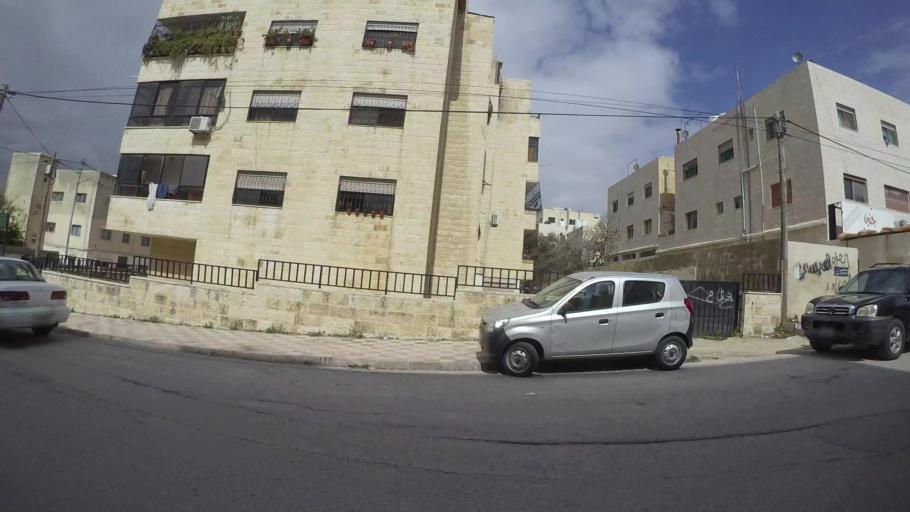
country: JO
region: Amman
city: Wadi as Sir
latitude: 31.9590
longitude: 35.8368
